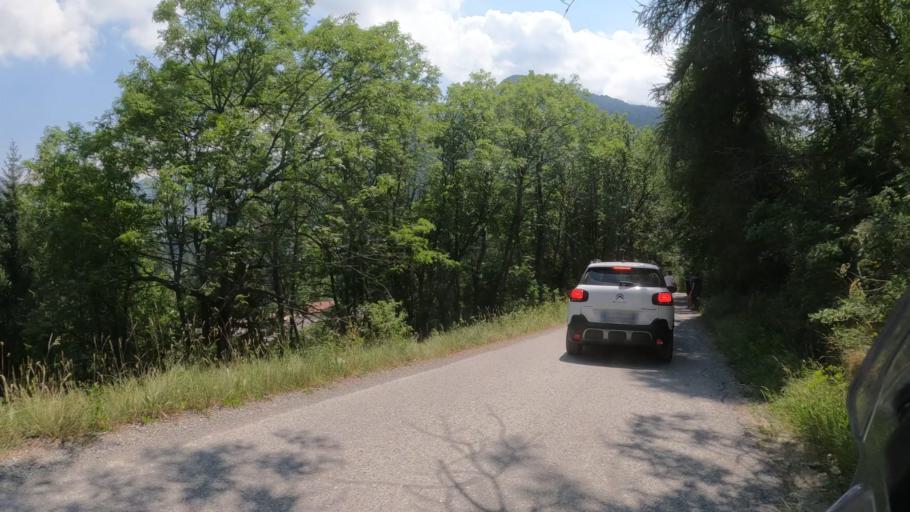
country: IT
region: Piedmont
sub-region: Provincia di Torino
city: Cesana Torinese
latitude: 44.9318
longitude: 6.8169
